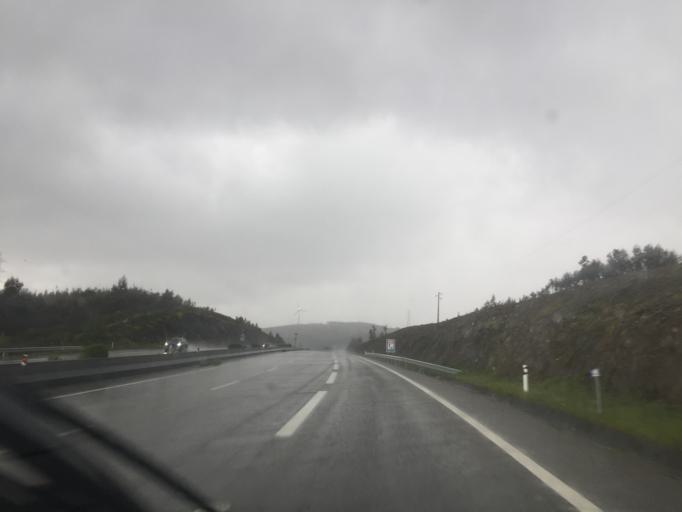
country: PT
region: Aveiro
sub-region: Sever do Vouga
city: Sever do Vouga
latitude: 40.6548
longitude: -8.3626
